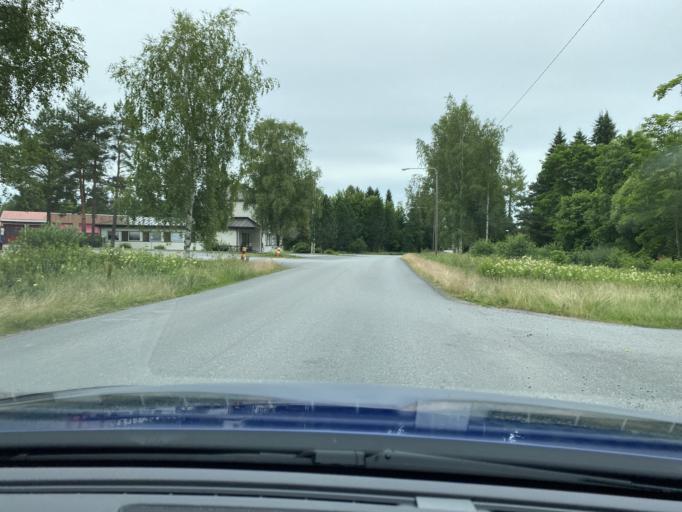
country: FI
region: Satakunta
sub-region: Rauma
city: Eura
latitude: 61.1095
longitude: 22.1441
